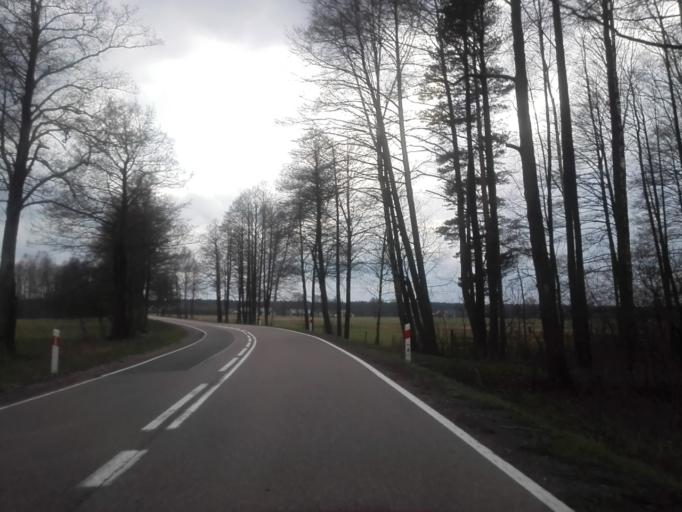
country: PL
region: Podlasie
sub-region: Powiat sejnenski
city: Krasnopol
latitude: 53.9452
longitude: 23.1887
